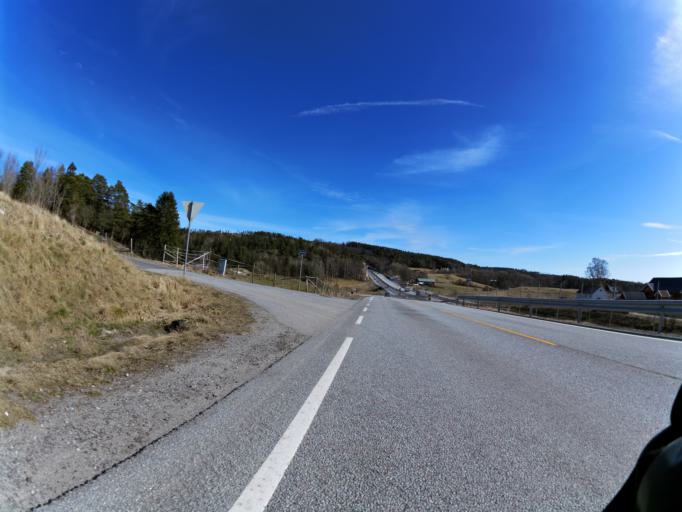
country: NO
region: Ostfold
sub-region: Fredrikstad
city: Fredrikstad
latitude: 59.3173
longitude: 10.9842
